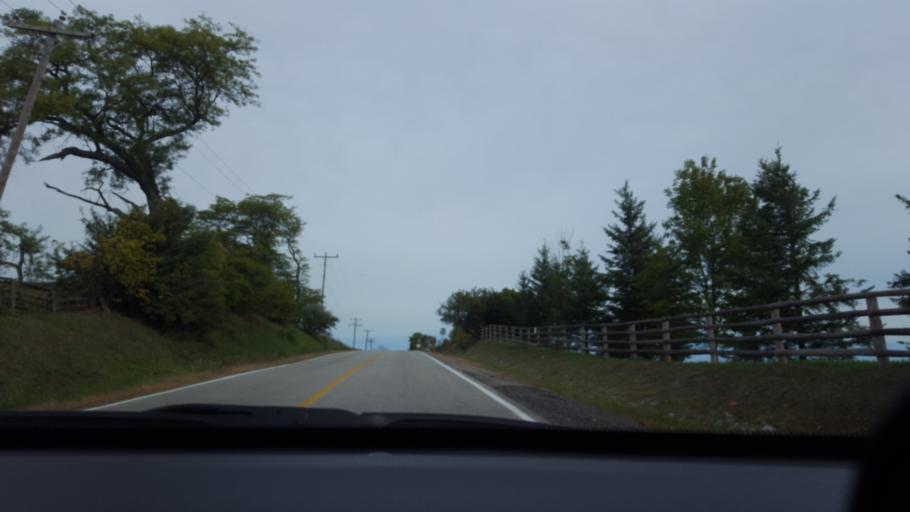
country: CA
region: Ontario
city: Newmarket
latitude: 44.0097
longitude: -79.5495
